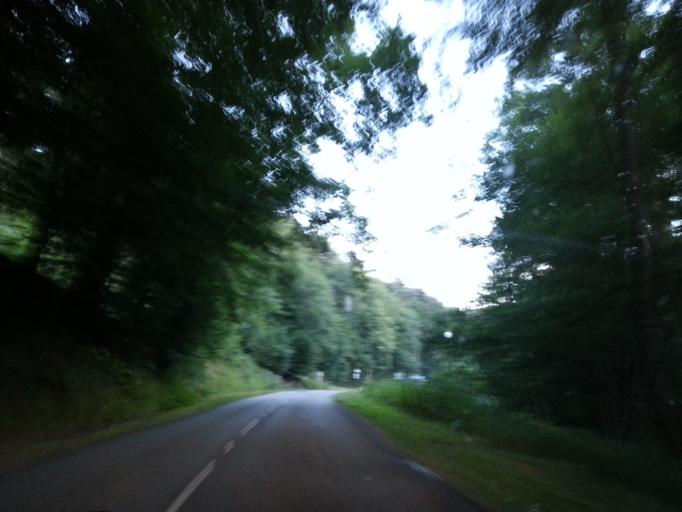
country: DE
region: Rheinland-Pfalz
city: Hirschthal
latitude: 49.0270
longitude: 7.7706
